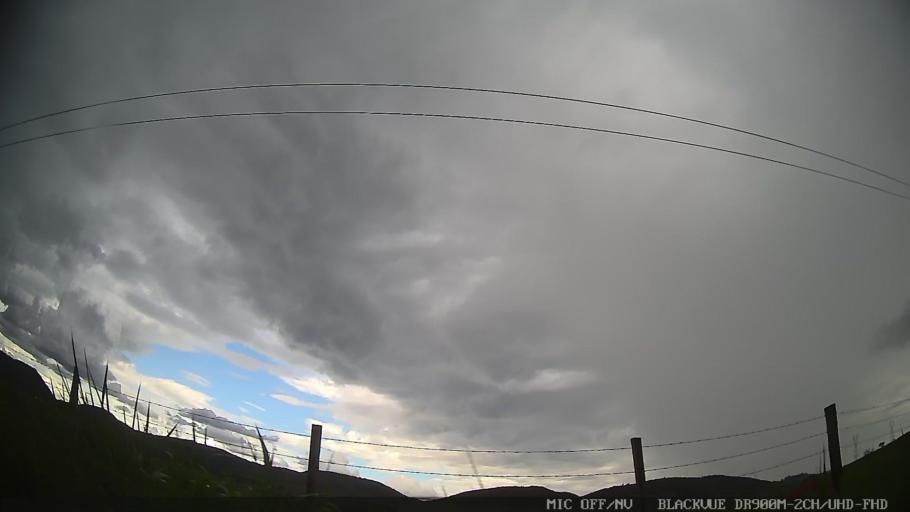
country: BR
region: Sao Paulo
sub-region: Pedreira
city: Pedreira
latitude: -22.6946
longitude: -46.8834
